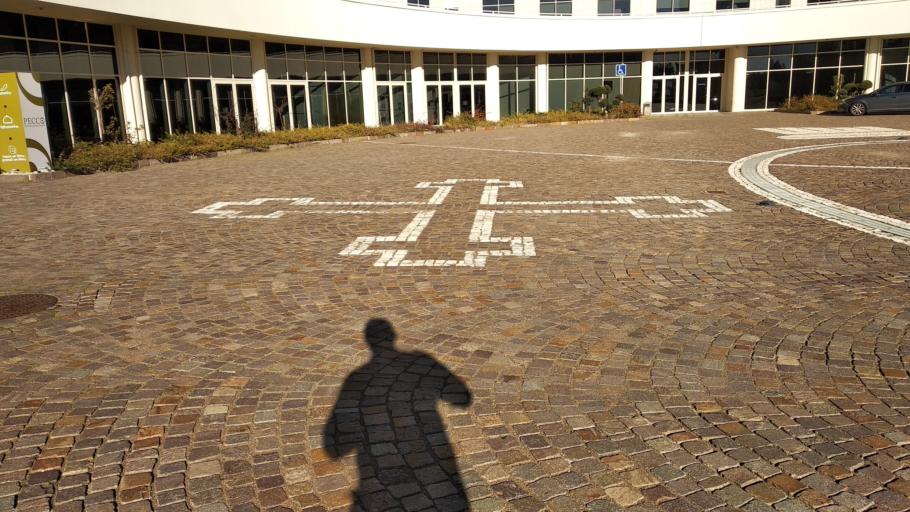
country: IT
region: Calabria
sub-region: Provincia di Catanzaro
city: Catanzaro
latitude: 38.8602
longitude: 16.5722
